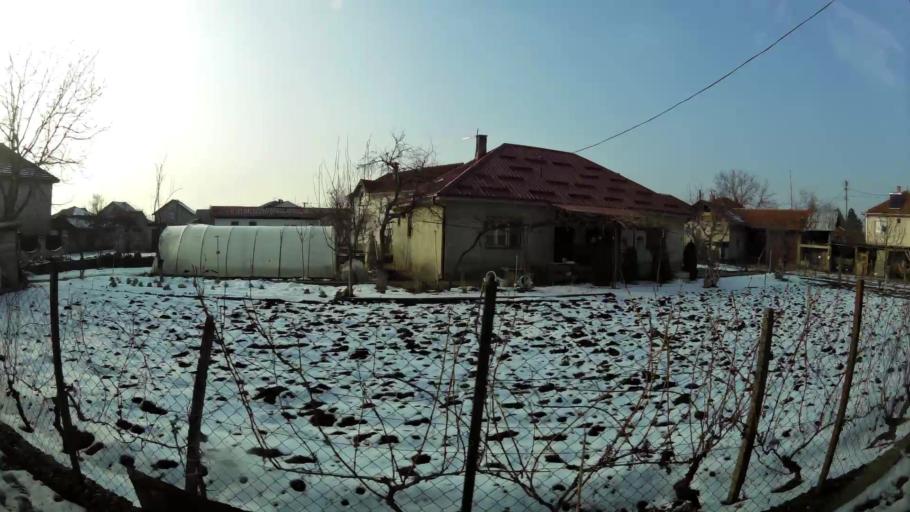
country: MK
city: Miladinovci
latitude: 41.9768
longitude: 21.6481
